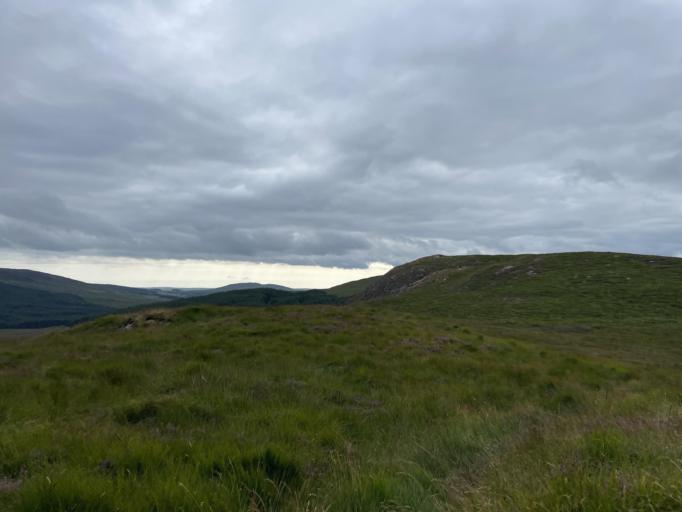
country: GB
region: Scotland
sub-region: Dumfries and Galloway
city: Newton Stewart
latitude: 54.9511
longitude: -4.2797
